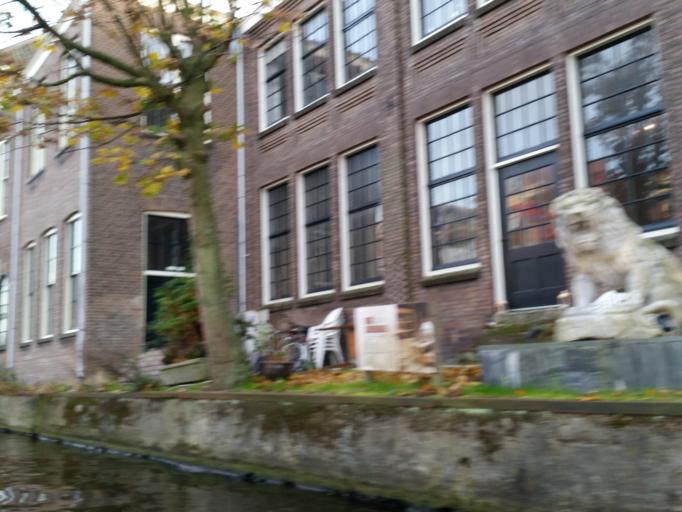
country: NL
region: South Holland
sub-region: Gemeente Leiden
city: Leiden
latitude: 52.1566
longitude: 4.4940
